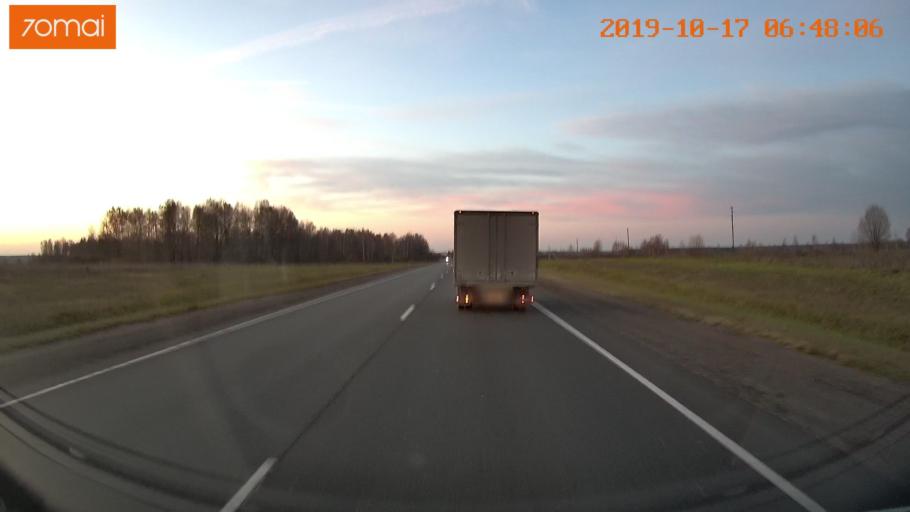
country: RU
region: Vladimir
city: Kideksha
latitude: 56.5274
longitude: 40.5574
